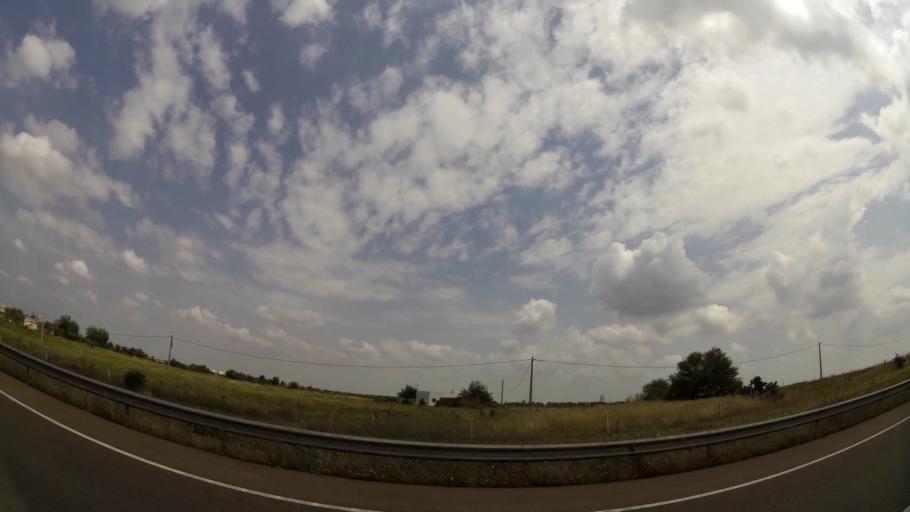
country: MA
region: Rabat-Sale-Zemmour-Zaer
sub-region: Khemisset
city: Tiflet
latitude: 33.9806
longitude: -6.5250
